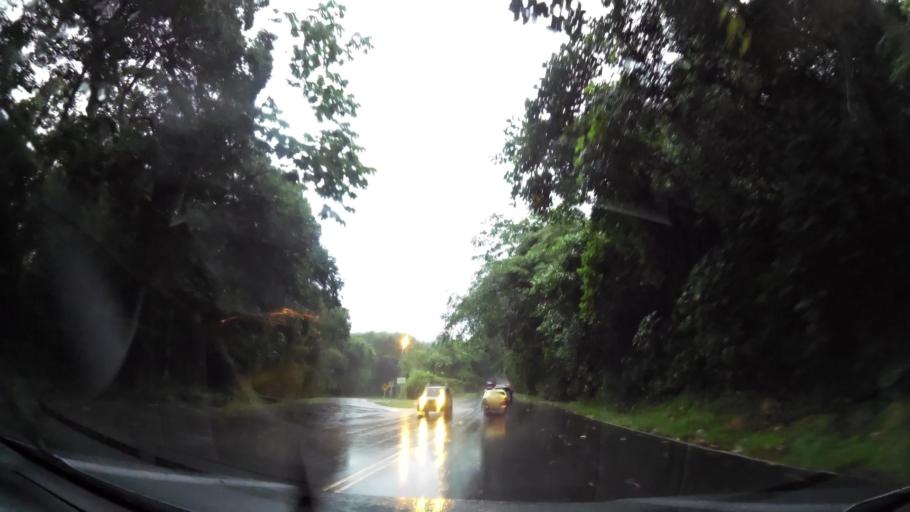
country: PA
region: Panama
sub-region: Distrito de Panama
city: Paraiso
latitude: 9.0051
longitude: -79.5917
